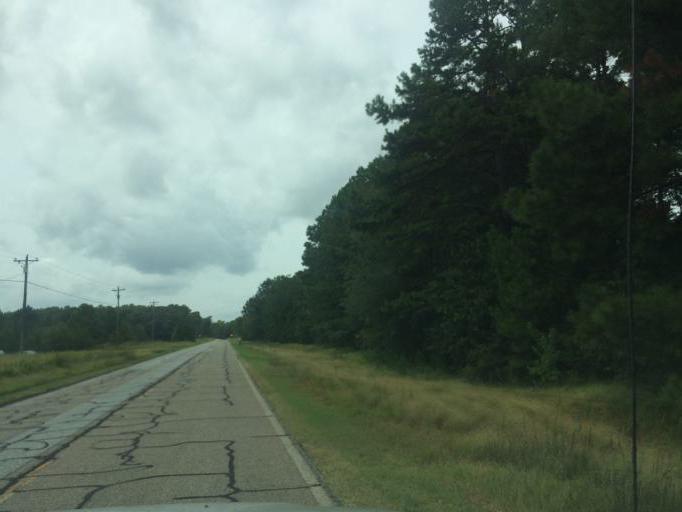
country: US
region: Georgia
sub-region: Hart County
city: Hartwell
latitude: 34.2875
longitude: -82.8499
